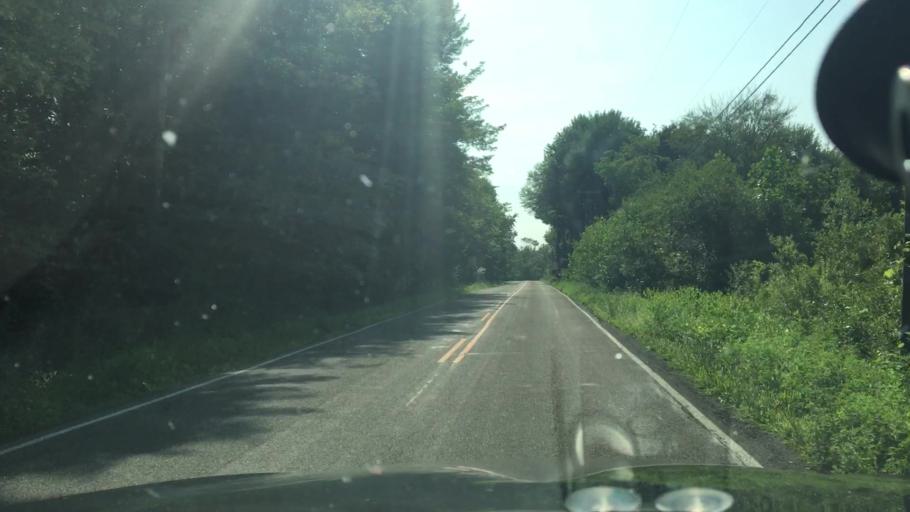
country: US
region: New York
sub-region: Erie County
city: North Collins
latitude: 42.6197
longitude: -78.9424
